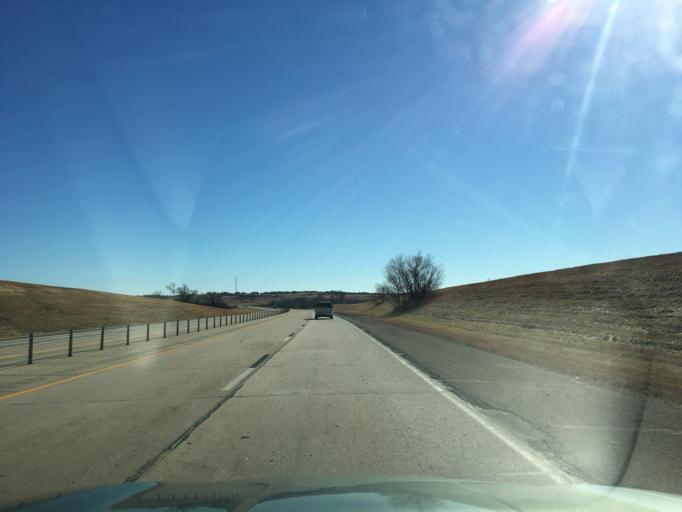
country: US
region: Oklahoma
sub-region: Payne County
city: Stillwater
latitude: 36.2608
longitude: -96.9730
